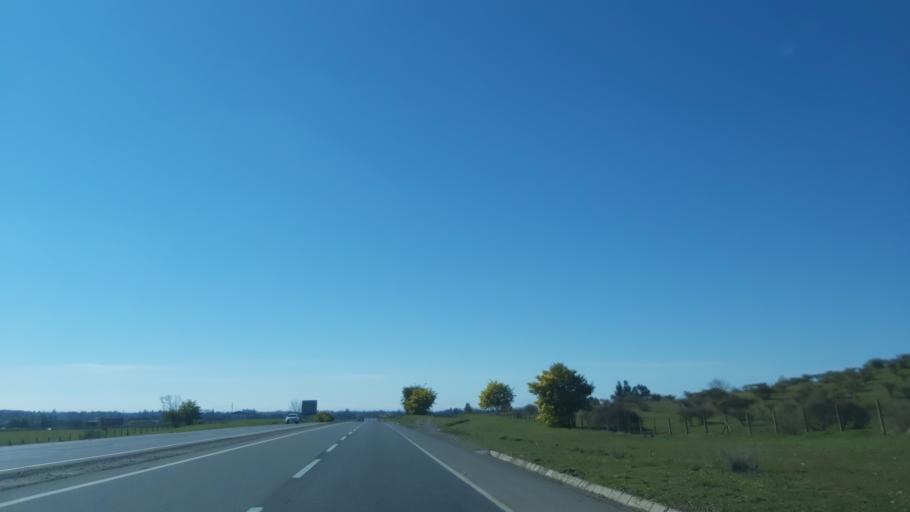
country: CL
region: Biobio
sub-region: Provincia de Nuble
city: Bulnes
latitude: -36.6596
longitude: -72.2544
